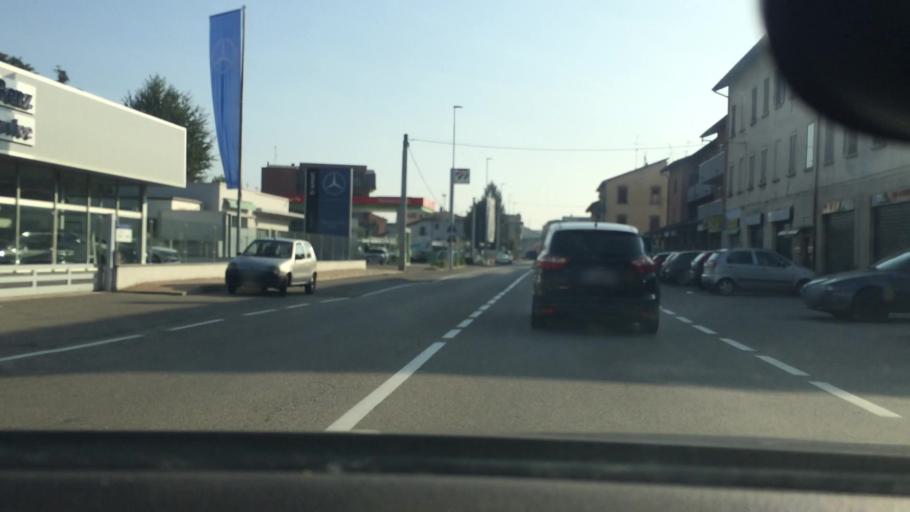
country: IT
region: Lombardy
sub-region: Provincia di Varese
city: Uboldo
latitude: 45.6136
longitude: 8.9983
